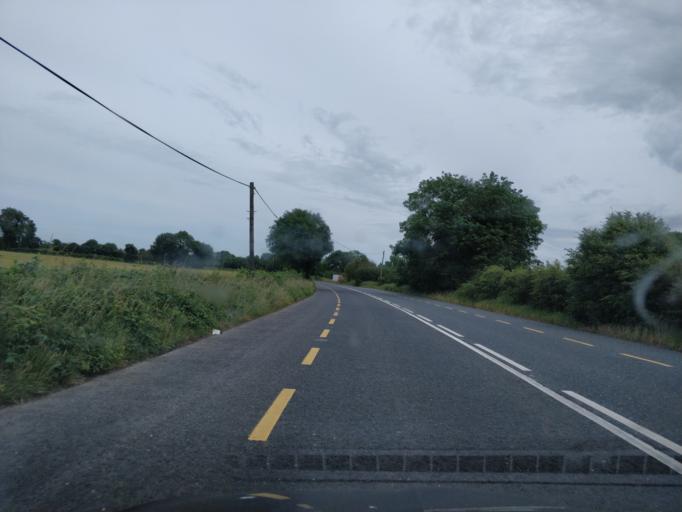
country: IE
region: Leinster
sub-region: Uibh Fhaili
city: Ferbane
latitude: 53.1683
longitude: -7.7567
